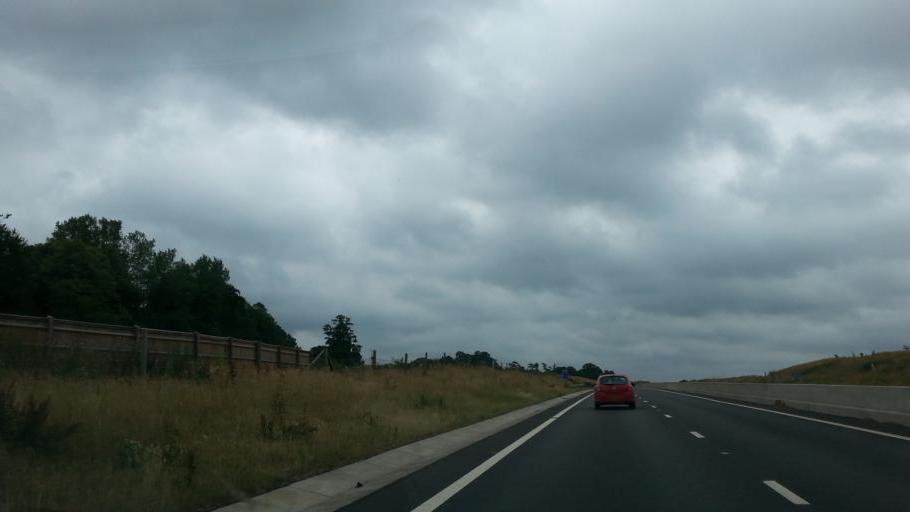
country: GB
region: England
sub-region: Nottinghamshire
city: Gotham
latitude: 52.8884
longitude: -1.2127
